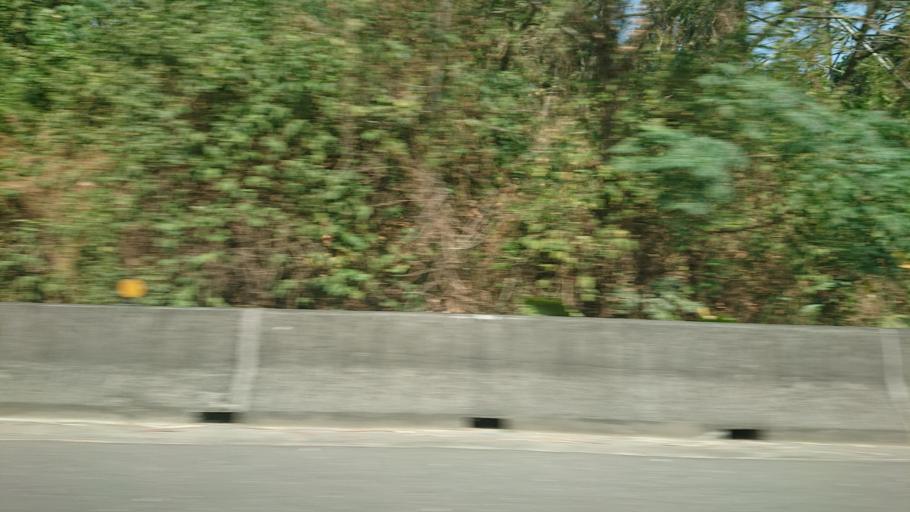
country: TW
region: Taiwan
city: Lugu
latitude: 23.7763
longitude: 120.6687
